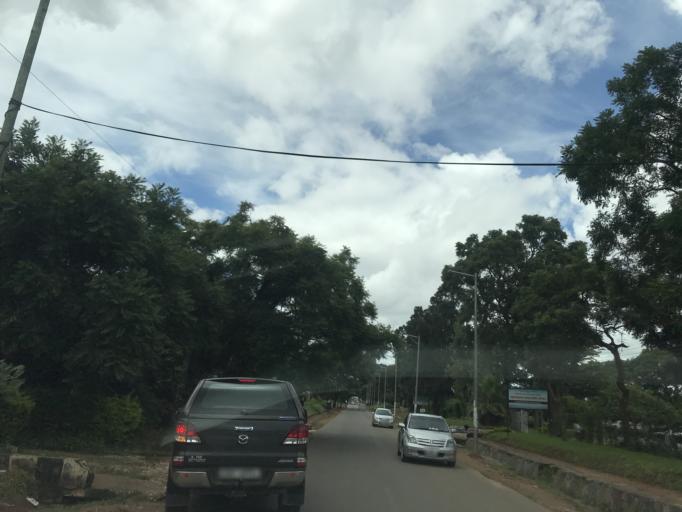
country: ZM
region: Lusaka
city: Lusaka
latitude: -15.4267
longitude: 28.3084
